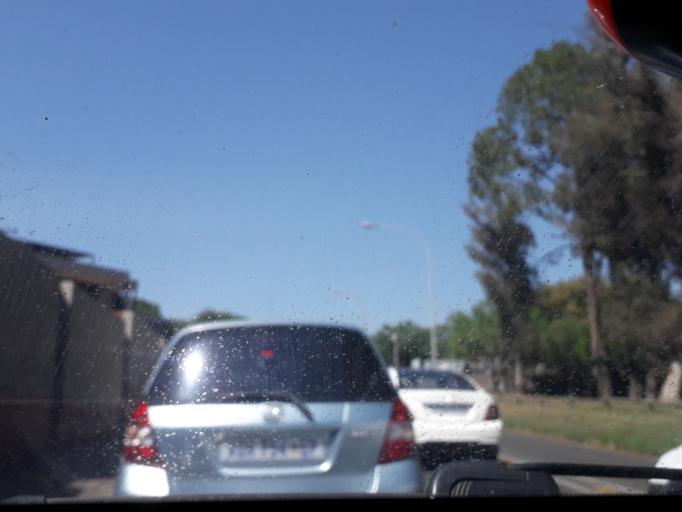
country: ZA
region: Gauteng
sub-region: City of Johannesburg Metropolitan Municipality
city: Johannesburg
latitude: -26.1406
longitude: 28.0672
